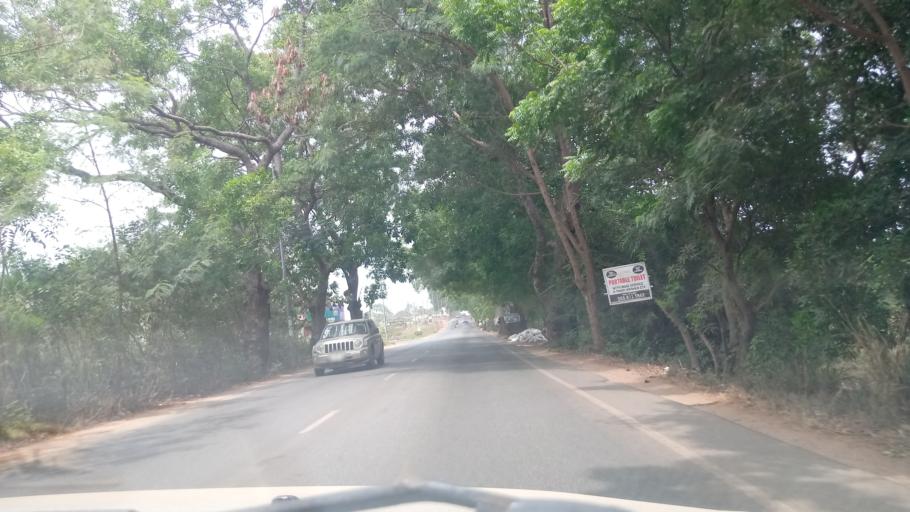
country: GH
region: Greater Accra
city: Dome
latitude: 5.6677
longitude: -0.2274
